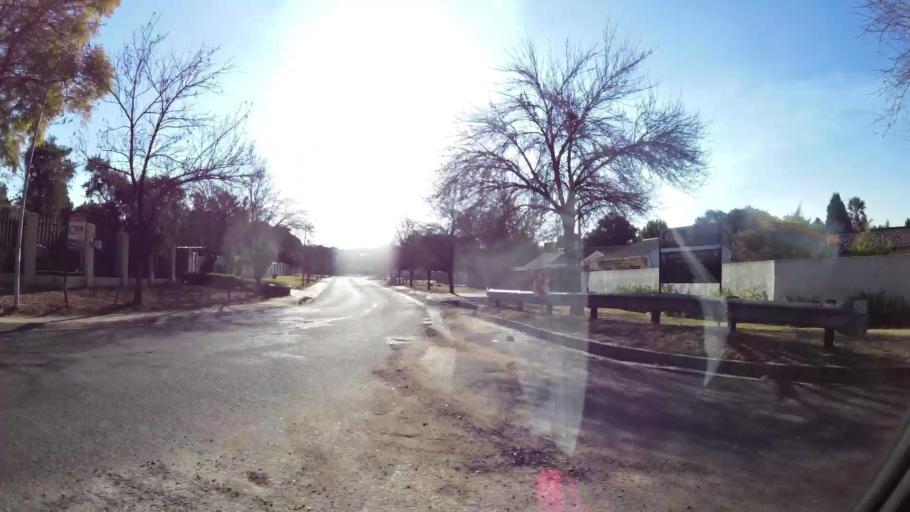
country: ZA
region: Gauteng
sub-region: City of Johannesburg Metropolitan Municipality
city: Roodepoort
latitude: -26.0902
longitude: 27.9630
